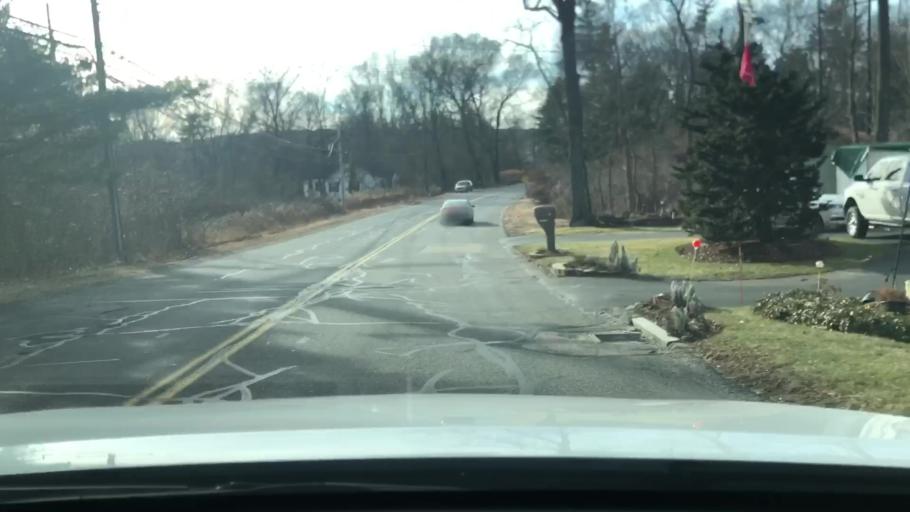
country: US
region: Massachusetts
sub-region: Worcester County
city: Millbury
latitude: 42.1933
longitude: -71.7385
